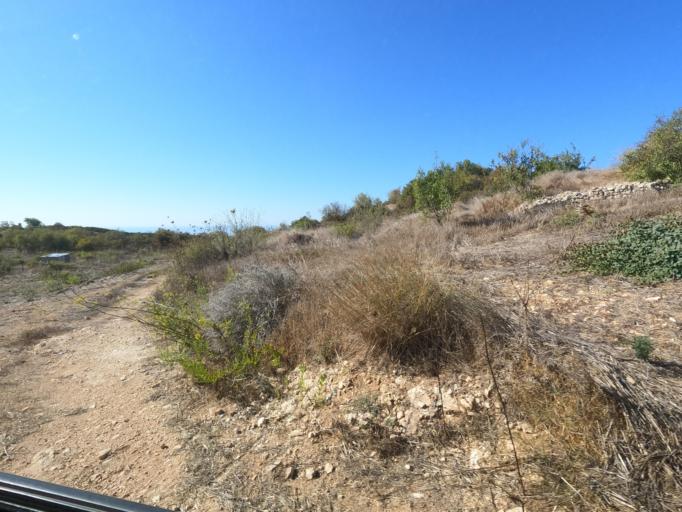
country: CY
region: Pafos
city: Mesogi
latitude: 34.8025
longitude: 32.4903
